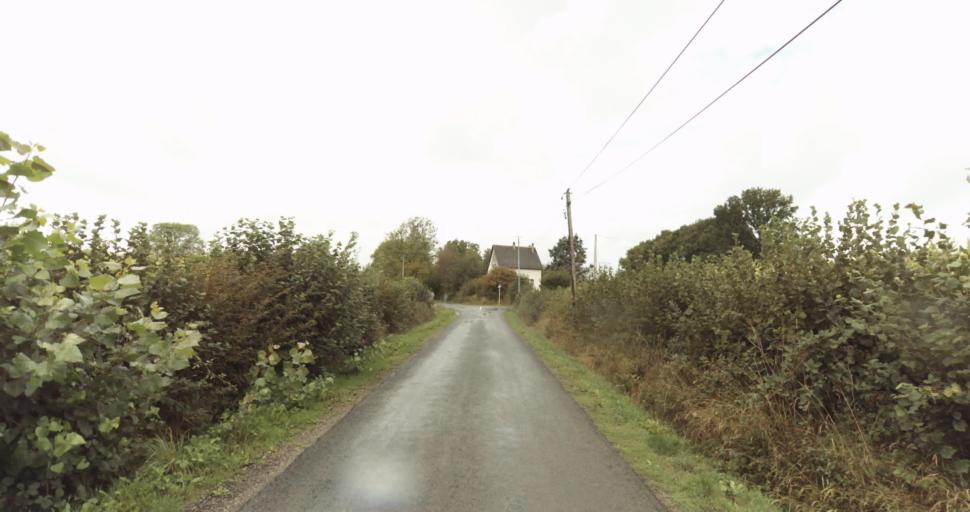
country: FR
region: Lower Normandy
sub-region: Departement de l'Orne
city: Sainte-Gauburge-Sainte-Colombe
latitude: 48.6909
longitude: 0.4123
